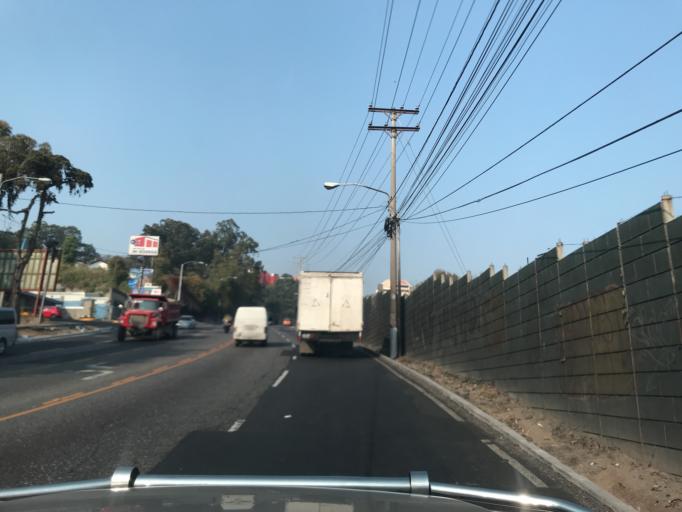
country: GT
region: Guatemala
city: Santa Catarina Pinula
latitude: 14.5674
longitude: -90.5285
